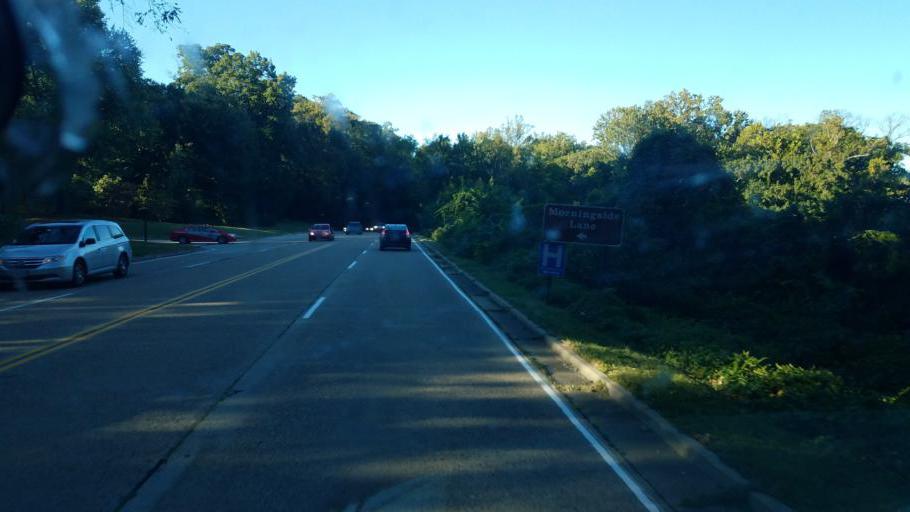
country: US
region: Virginia
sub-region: Fairfax County
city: Fort Hunt
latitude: 38.7511
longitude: -77.0497
